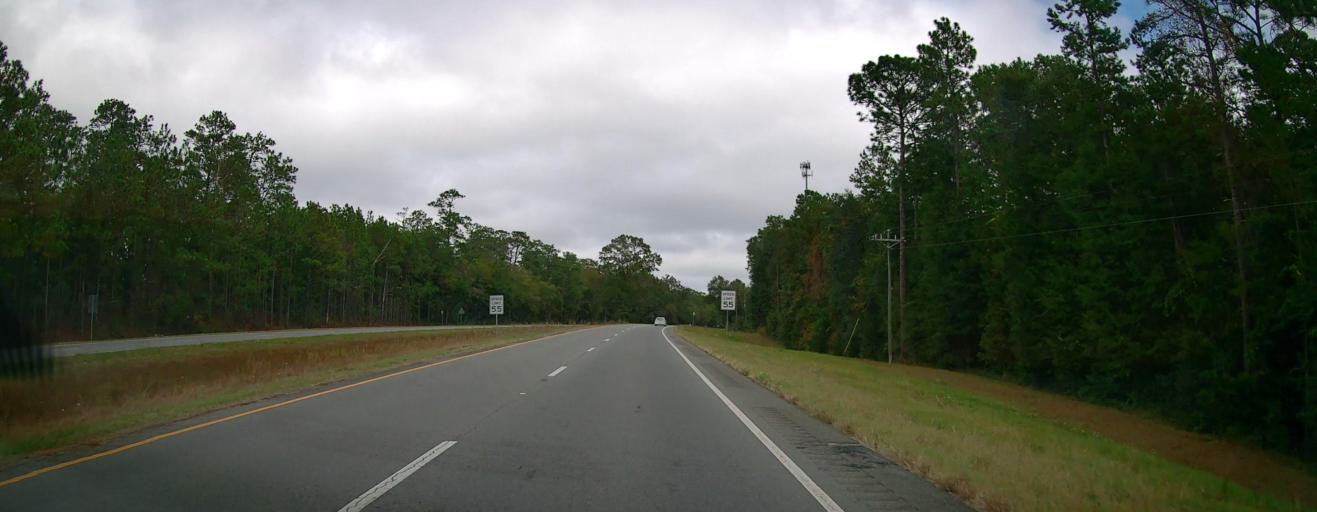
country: US
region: Georgia
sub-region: Grady County
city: Cairo
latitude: 30.7054
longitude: -84.1448
